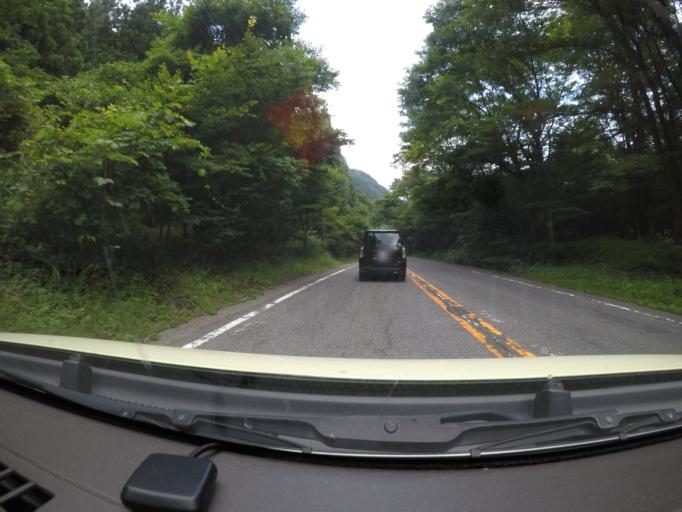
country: JP
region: Tochigi
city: Nikko
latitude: 36.7391
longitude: 139.5327
